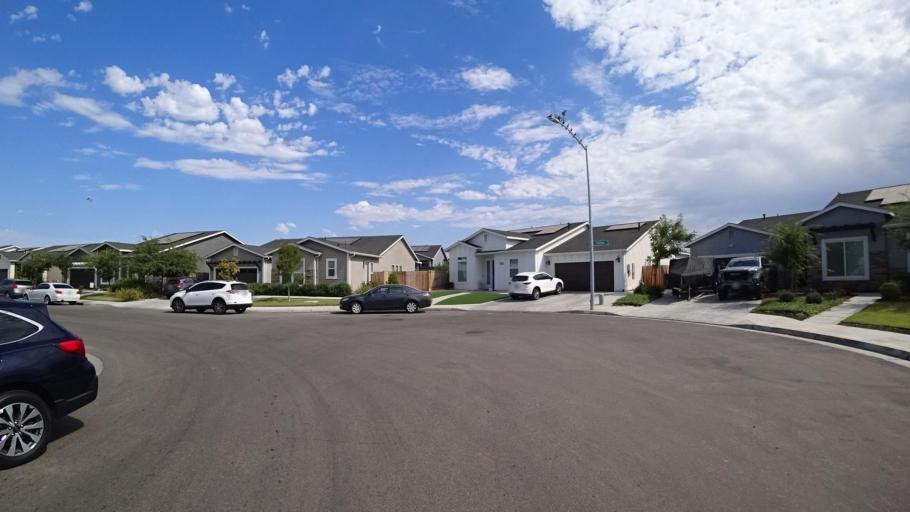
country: US
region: California
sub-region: Fresno County
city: Tarpey Village
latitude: 36.7833
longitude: -119.6738
